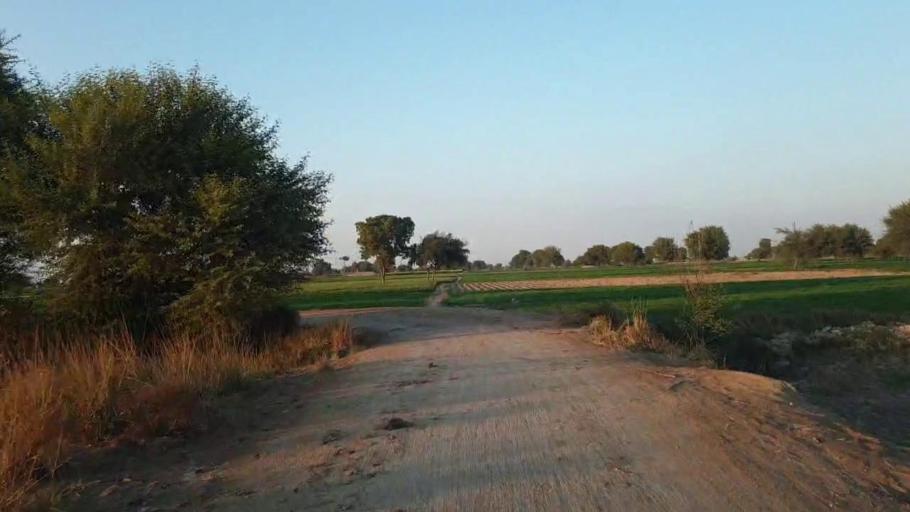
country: PK
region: Sindh
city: Shahpur Chakar
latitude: 26.1602
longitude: 68.5333
